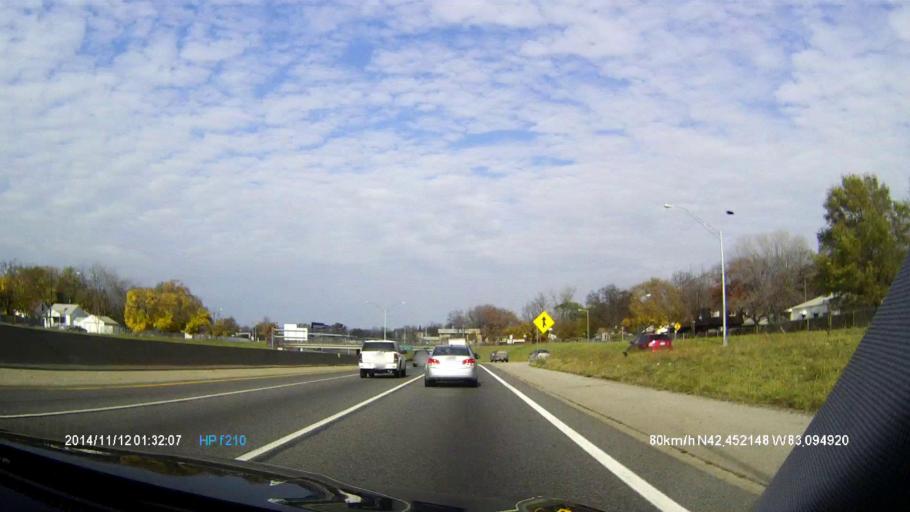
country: US
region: Michigan
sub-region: Oakland County
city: Hazel Park
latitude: 42.4524
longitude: -83.0951
